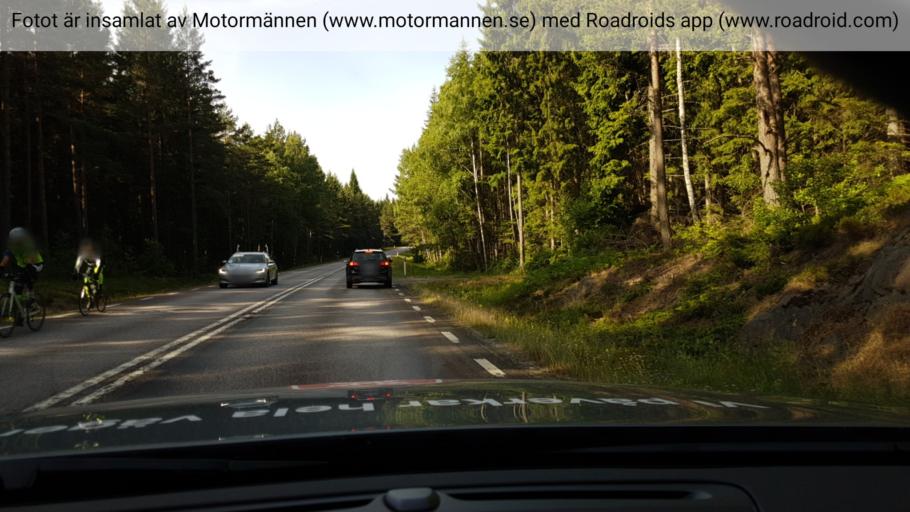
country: SE
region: OErebro
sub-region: Askersunds Kommun
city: Askersund
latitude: 58.7361
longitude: 14.7766
